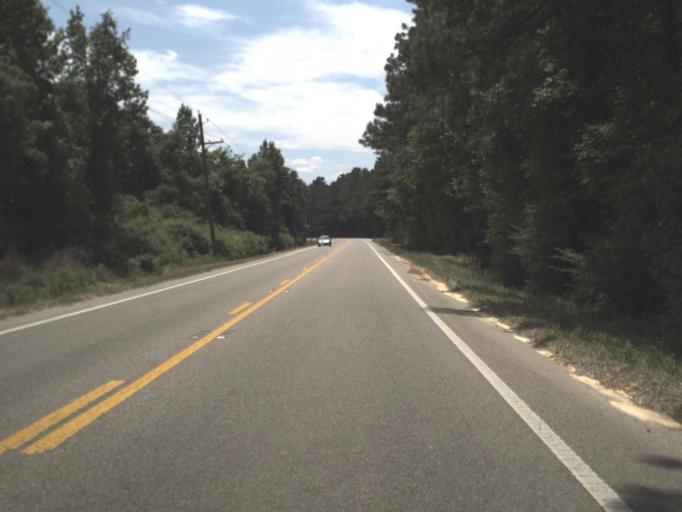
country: US
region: Florida
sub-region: Calhoun County
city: Blountstown
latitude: 30.5350
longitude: -85.1325
